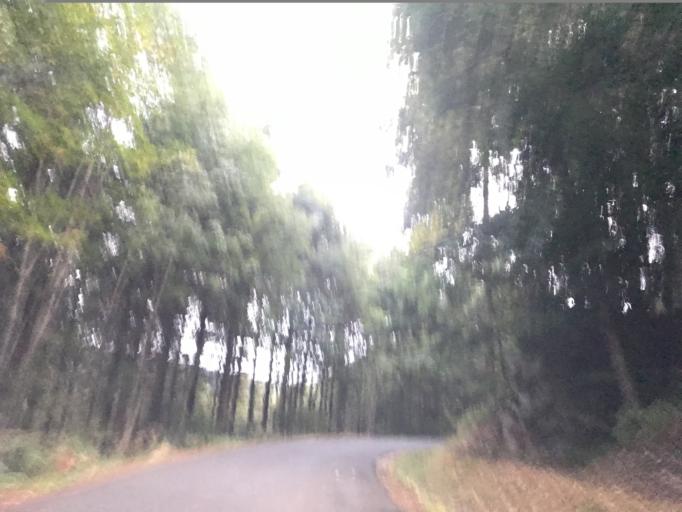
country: FR
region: Auvergne
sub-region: Departement du Puy-de-Dome
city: Celles-sur-Durolle
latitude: 45.8238
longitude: 3.6592
